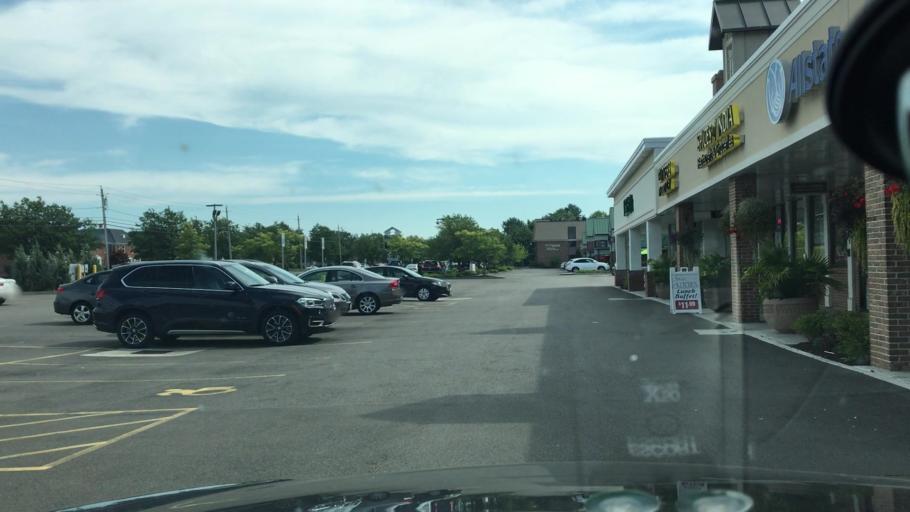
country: US
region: New York
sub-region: Erie County
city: Williamsville
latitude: 42.9765
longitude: -78.7402
